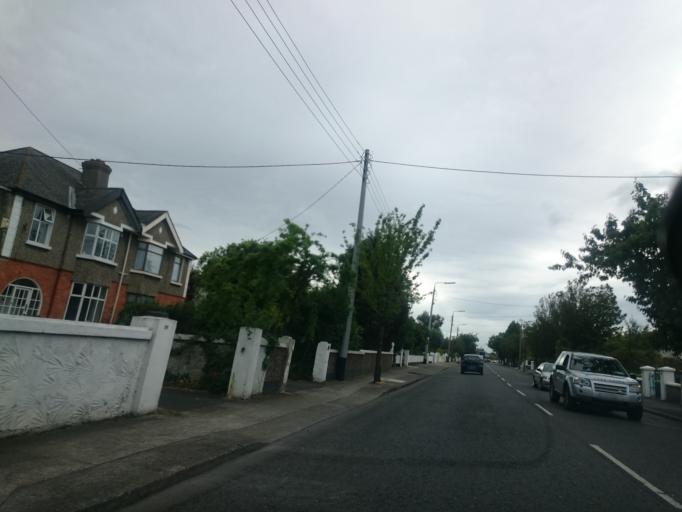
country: IE
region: Leinster
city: Templeogue
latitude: 53.3131
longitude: -6.3063
